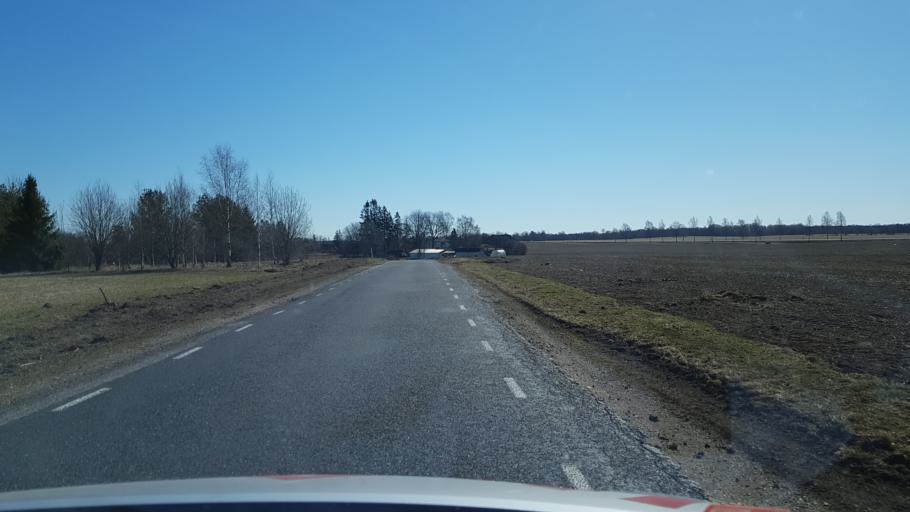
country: EE
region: Laeaene-Virumaa
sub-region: Haljala vald
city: Haljala
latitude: 59.4360
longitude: 26.1835
